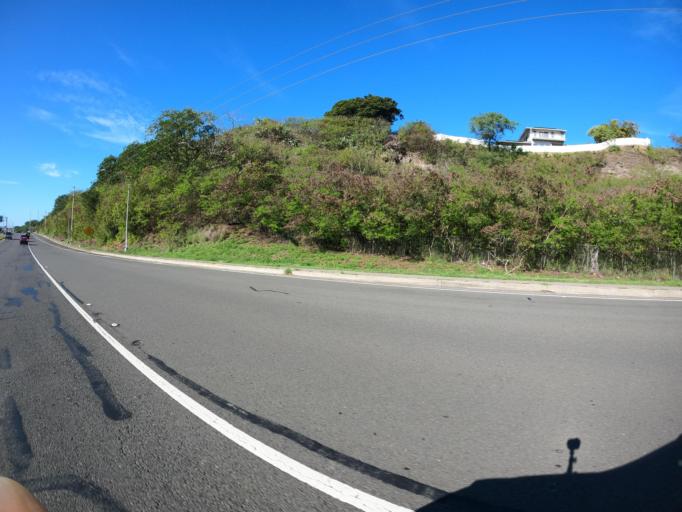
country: US
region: Hawaii
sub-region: Honolulu County
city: Halawa Heights
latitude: 21.3479
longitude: -157.8974
